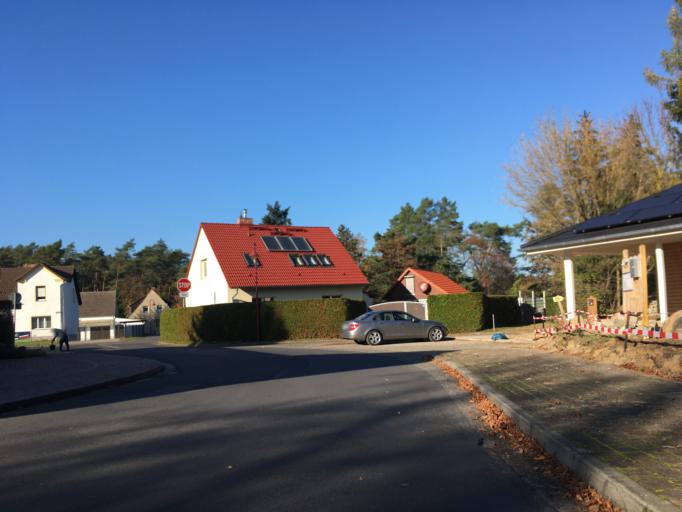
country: DE
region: Brandenburg
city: Reichenwalde
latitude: 52.2909
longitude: 13.9862
